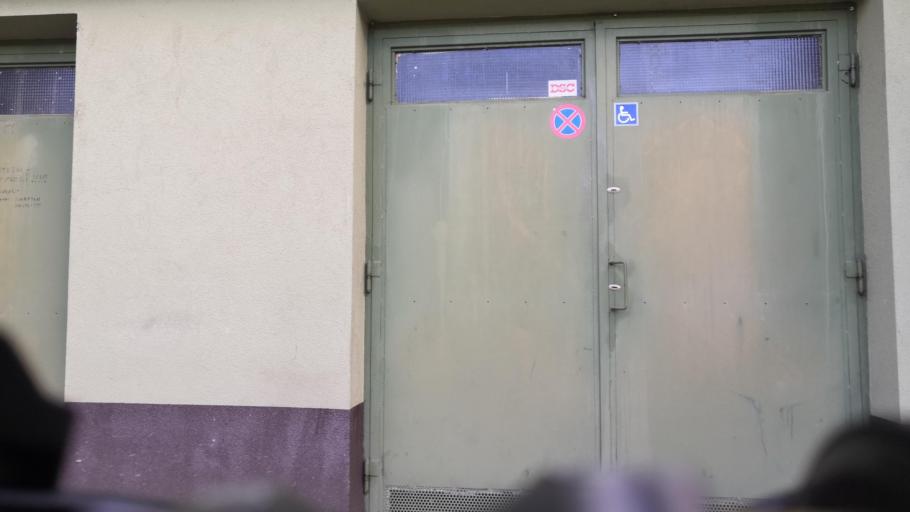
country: HU
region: Csongrad
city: Szeged
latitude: 46.2737
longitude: 20.1533
